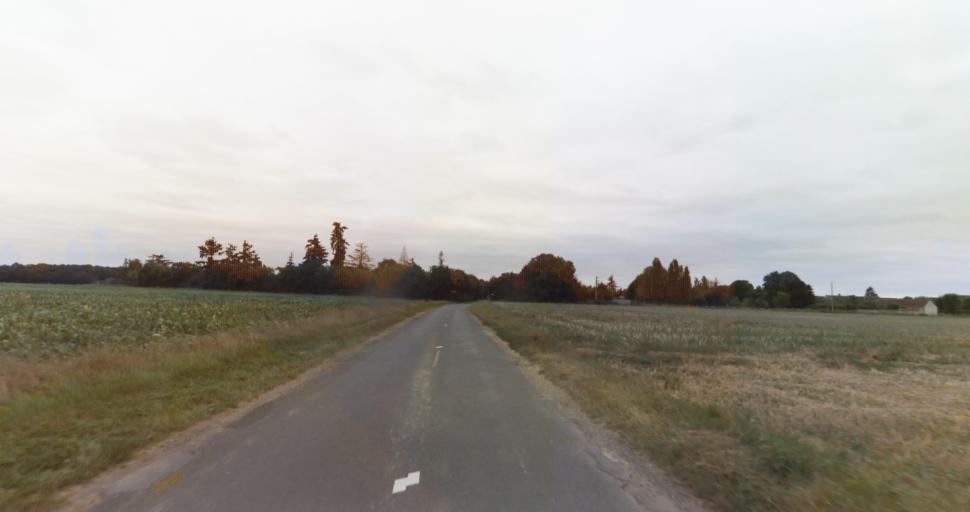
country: FR
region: Haute-Normandie
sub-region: Departement de l'Eure
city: Saint-Germain-sur-Avre
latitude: 48.8194
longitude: 1.2889
